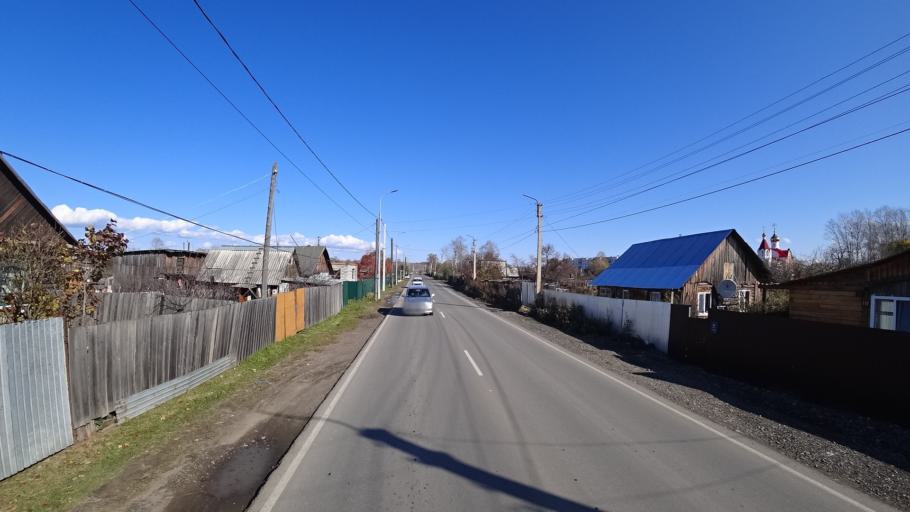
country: RU
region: Khabarovsk Krai
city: Amursk
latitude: 50.1022
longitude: 136.5108
